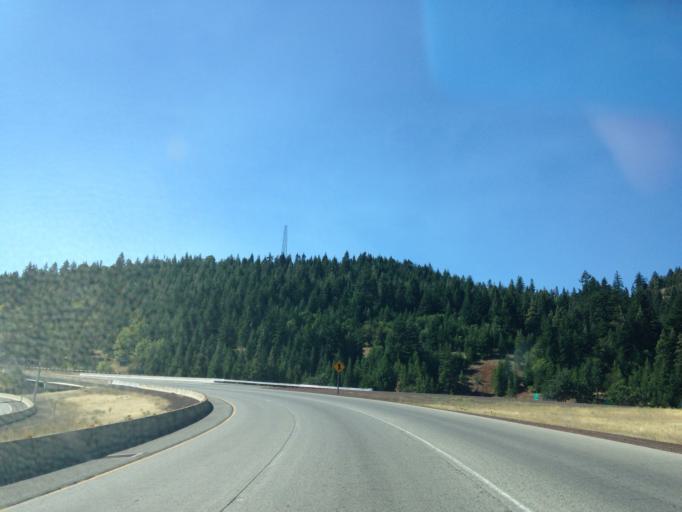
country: US
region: Oregon
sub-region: Jackson County
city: Ashland
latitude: 42.0749
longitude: -122.6057
